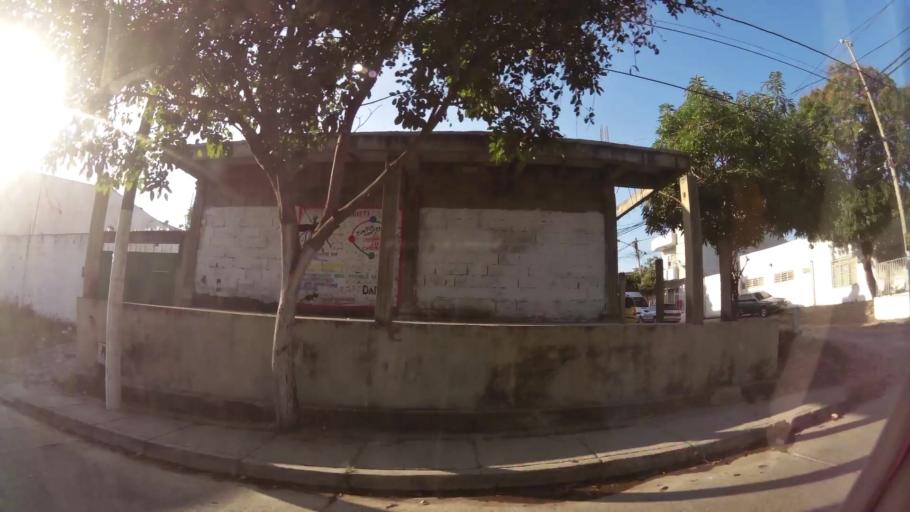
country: CO
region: Bolivar
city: Cartagena
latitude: 10.3966
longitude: -75.4817
